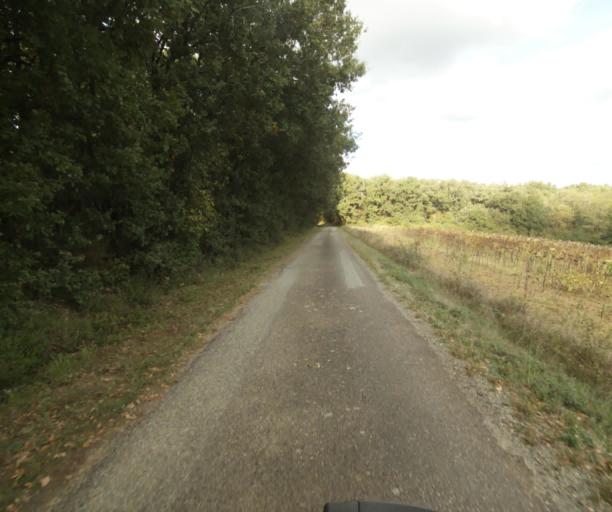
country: FR
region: Midi-Pyrenees
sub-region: Departement de la Haute-Garonne
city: Launac
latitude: 43.8319
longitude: 1.1176
